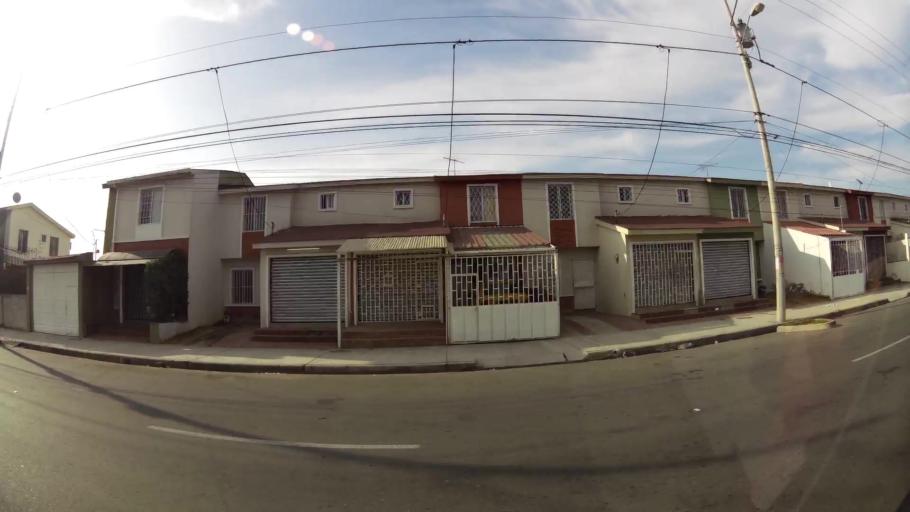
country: EC
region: Guayas
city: Eloy Alfaro
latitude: -2.0679
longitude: -79.8980
